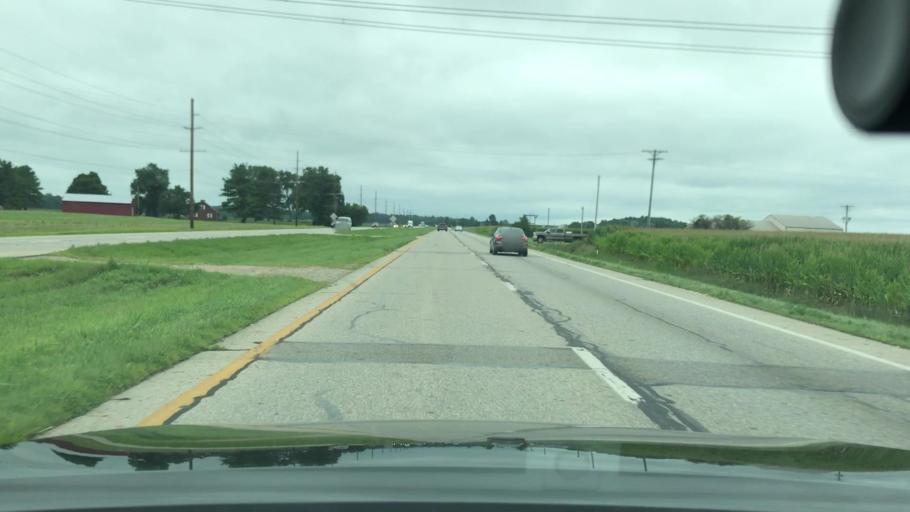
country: US
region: Ohio
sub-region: Pickaway County
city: Logan Elm Village
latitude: 39.5485
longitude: -82.9627
